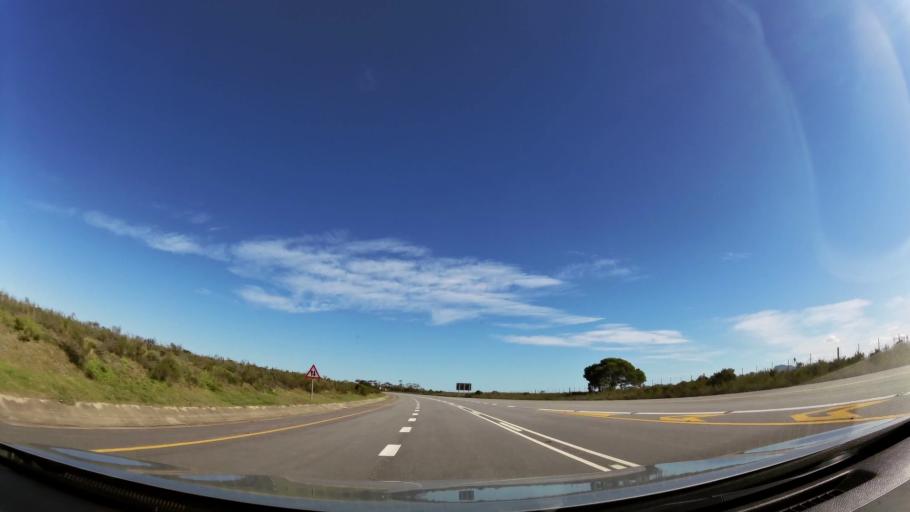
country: ZA
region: Eastern Cape
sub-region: Cacadu District Municipality
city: Kruisfontein
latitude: -34.0313
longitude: 24.5962
